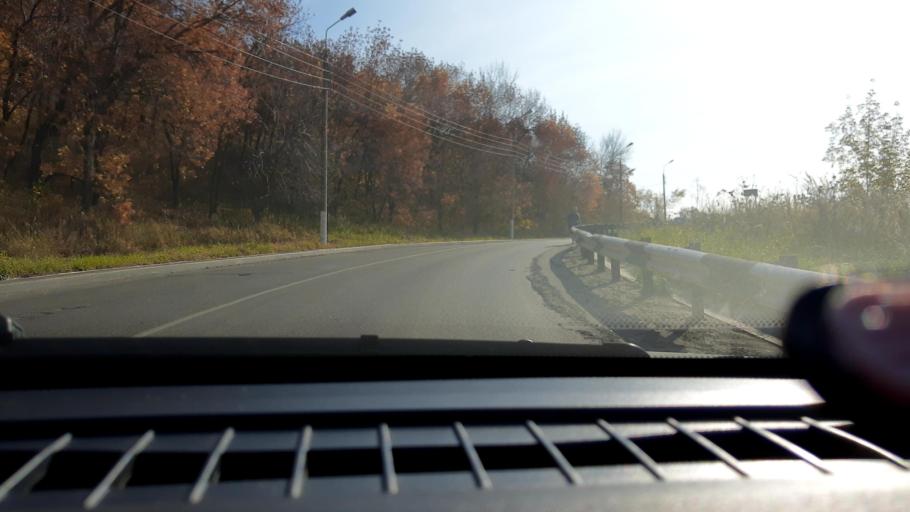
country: RU
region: Nizjnij Novgorod
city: Kstovo
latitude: 56.1573
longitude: 44.2481
